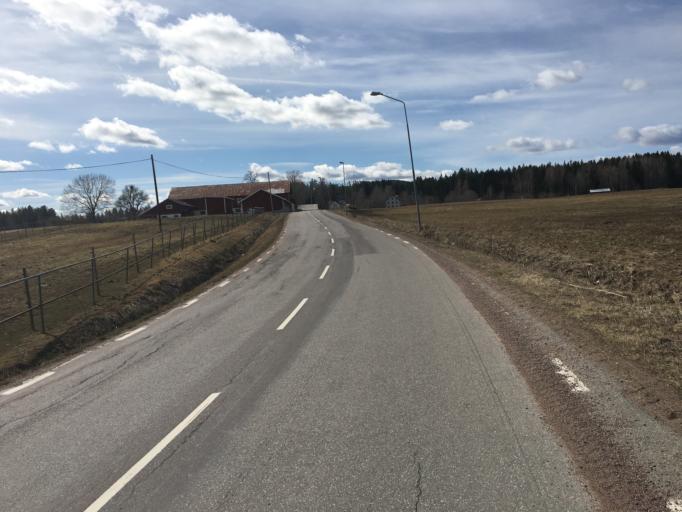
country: SE
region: Gaevleborg
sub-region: Hofors Kommun
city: Hofors
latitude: 60.5045
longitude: 16.4475
